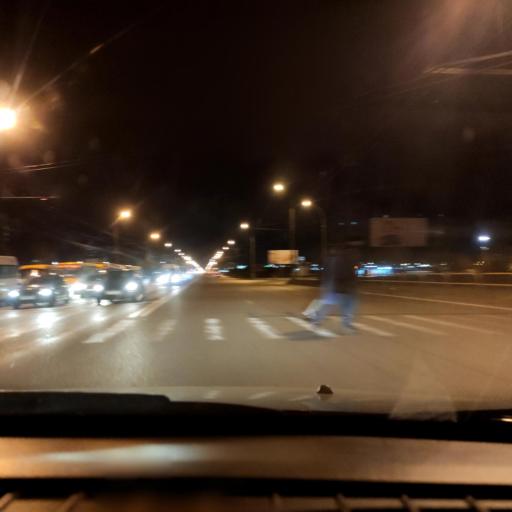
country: RU
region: Samara
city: Tol'yatti
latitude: 53.5469
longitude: 49.3616
